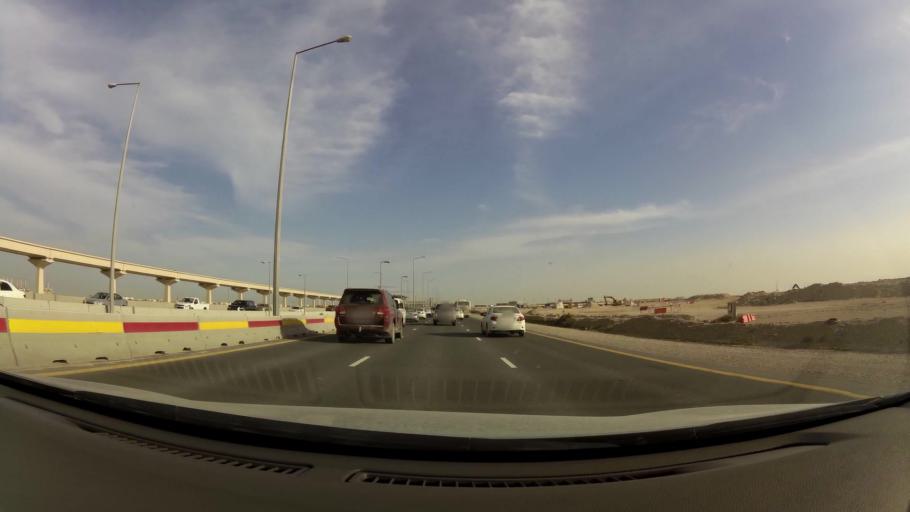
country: QA
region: Al Wakrah
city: Al Wakrah
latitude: 25.2009
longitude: 51.5911
